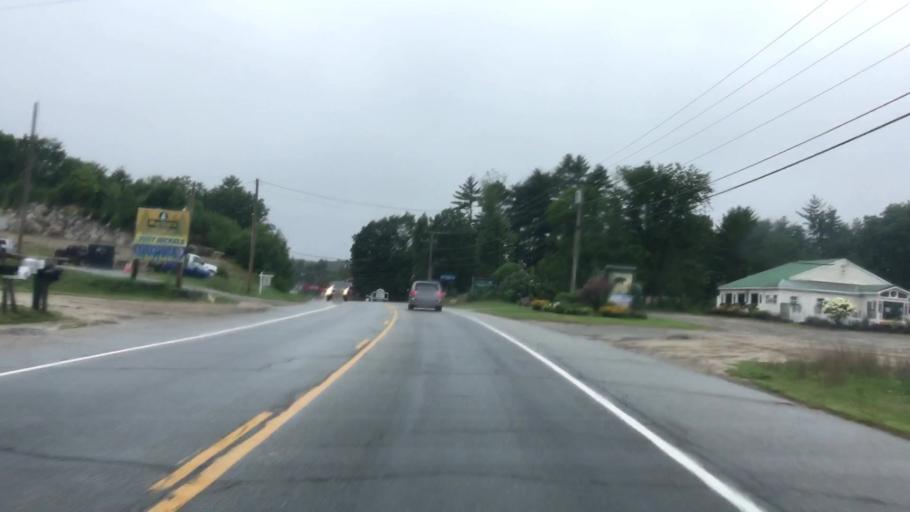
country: US
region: Maine
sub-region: Cumberland County
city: Raymond
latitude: 43.9630
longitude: -70.5731
